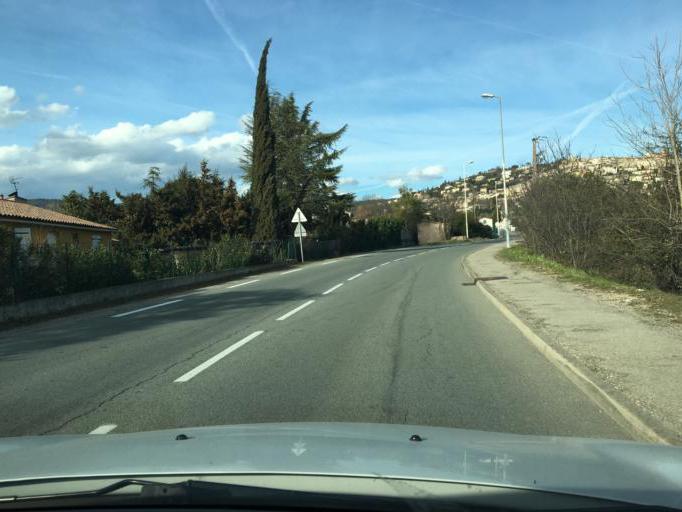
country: FR
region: Provence-Alpes-Cote d'Azur
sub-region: Departement du Var
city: Fayence
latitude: 43.6163
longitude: 6.6875
